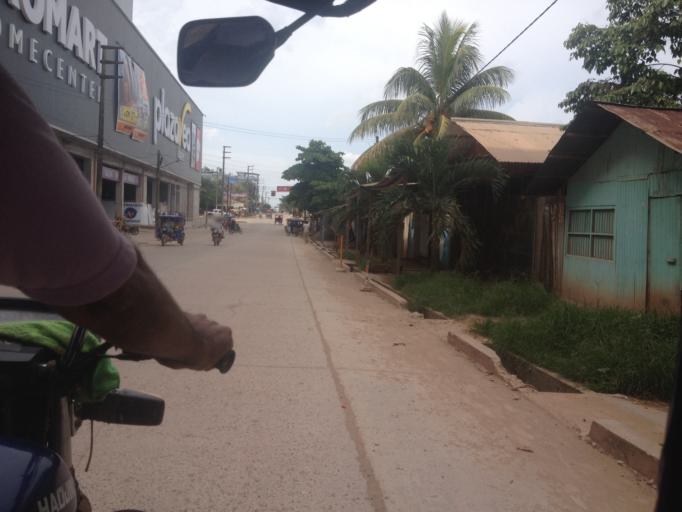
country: PE
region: Ucayali
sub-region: Provincia de Coronel Portillo
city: Pucallpa
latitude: -8.3847
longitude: -74.5557
